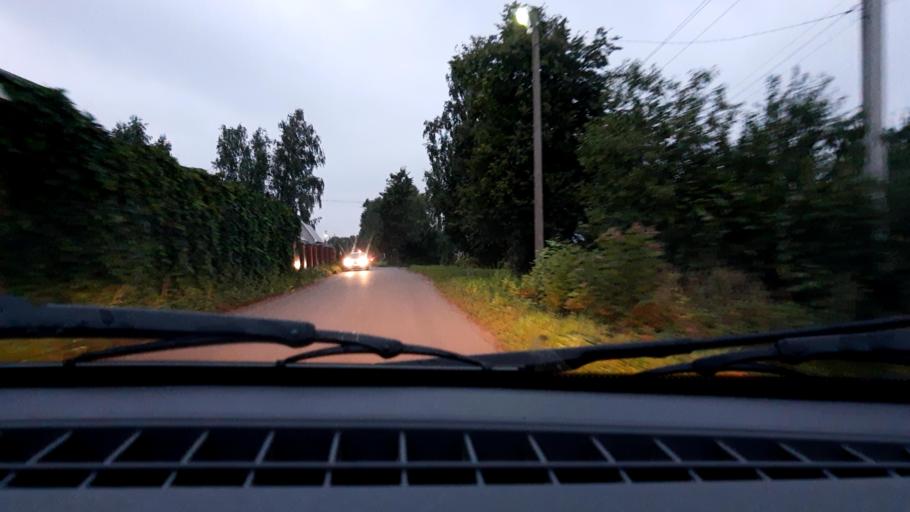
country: RU
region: Bashkortostan
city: Mikhaylovka
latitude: 54.8595
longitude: 55.8044
